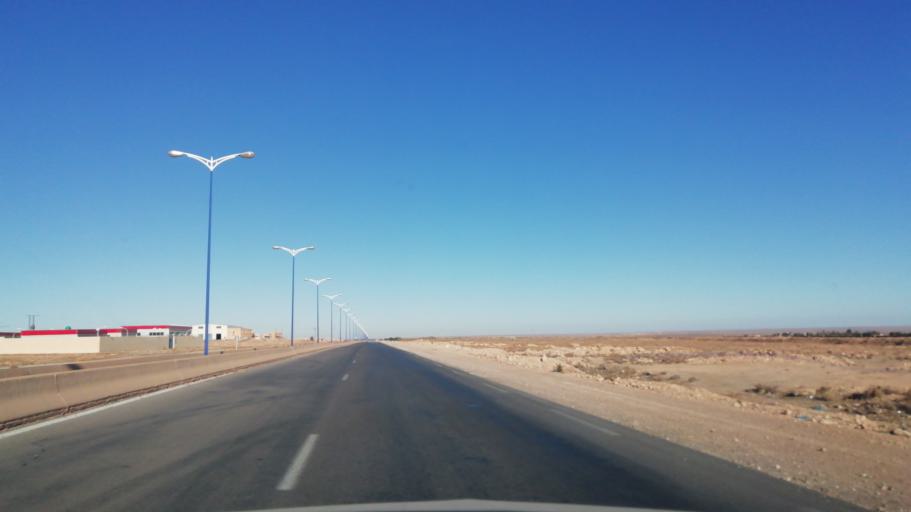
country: DZ
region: Wilaya de Naama
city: Naama
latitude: 33.5432
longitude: -0.2520
